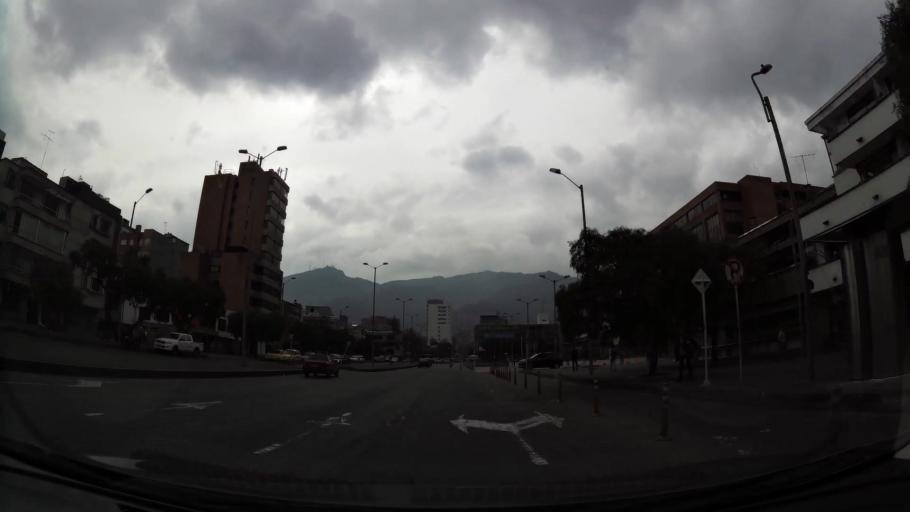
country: CO
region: Bogota D.C.
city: Barrio San Luis
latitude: 4.6707
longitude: -74.0567
